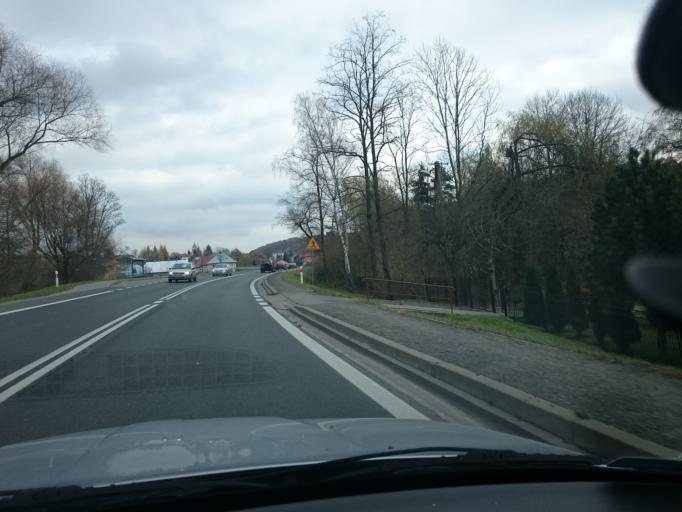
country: PL
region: Lesser Poland Voivodeship
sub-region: Powiat krakowski
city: Michalowice
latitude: 50.1733
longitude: 19.9802
